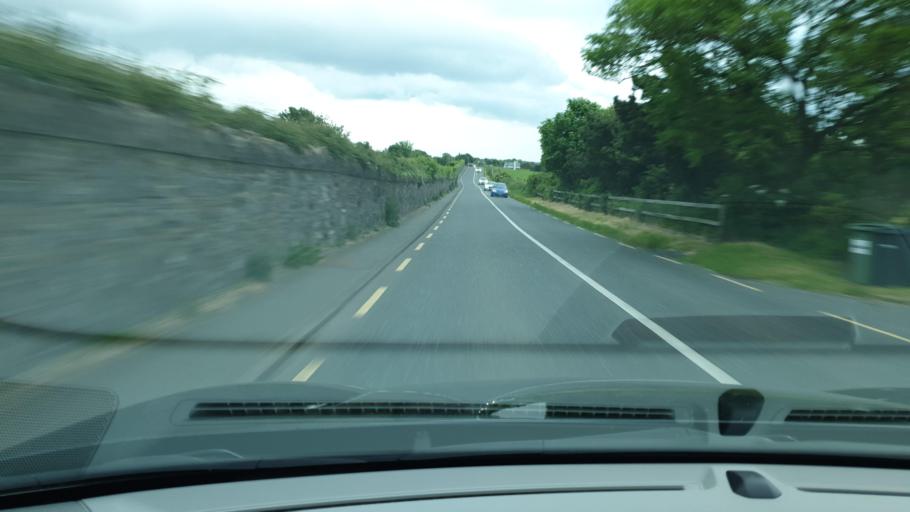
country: IE
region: Leinster
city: Balbriggan
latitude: 53.5976
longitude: -6.1624
